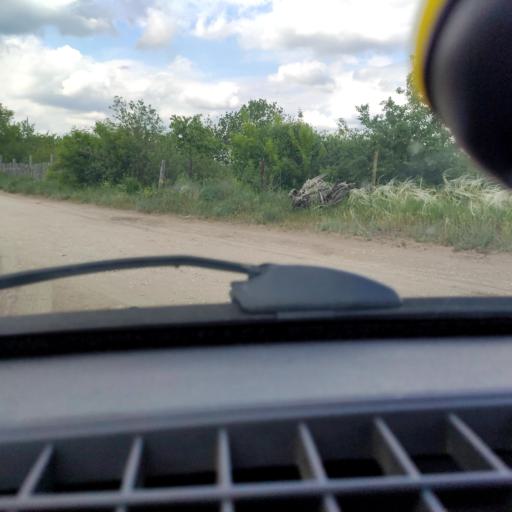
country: RU
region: Samara
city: Povolzhskiy
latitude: 53.6324
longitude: 49.6662
